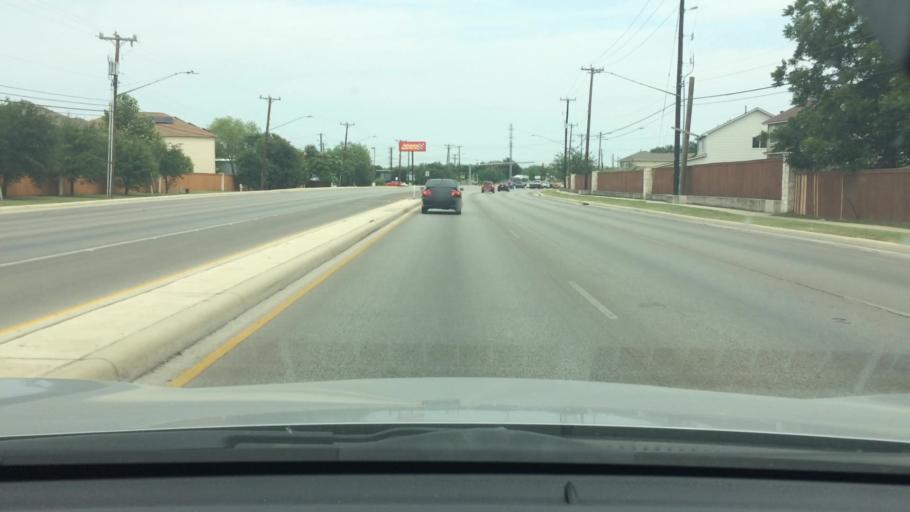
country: US
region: Texas
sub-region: Bexar County
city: Leon Valley
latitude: 29.4753
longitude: -98.6573
